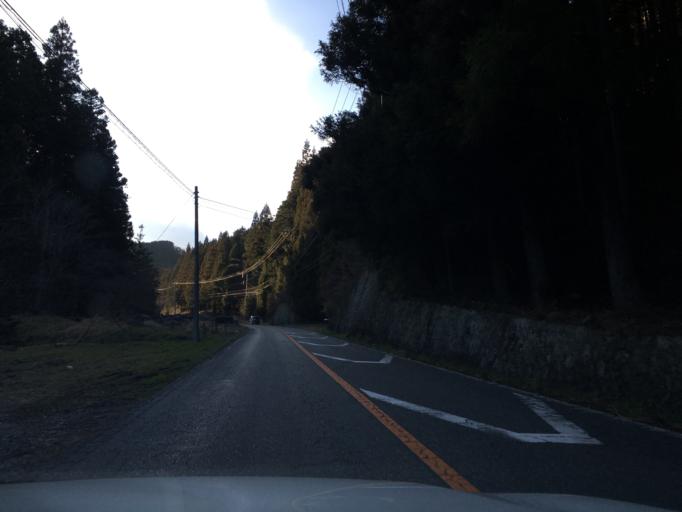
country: JP
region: Tochigi
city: Otawara
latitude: 36.8472
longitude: 140.1840
